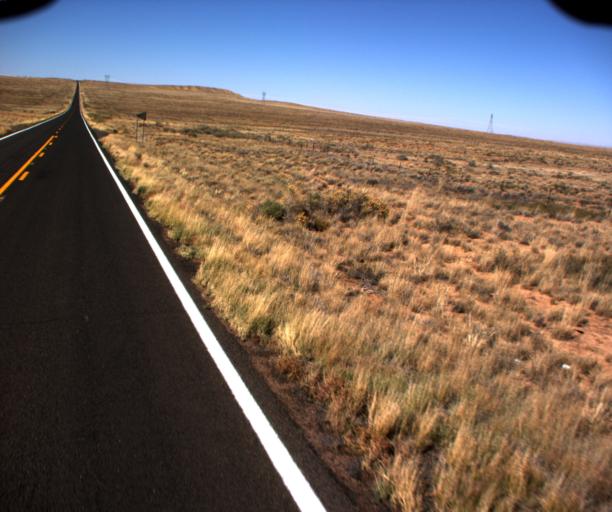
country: US
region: Arizona
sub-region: Coconino County
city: Tuba City
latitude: 35.9426
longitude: -110.9101
